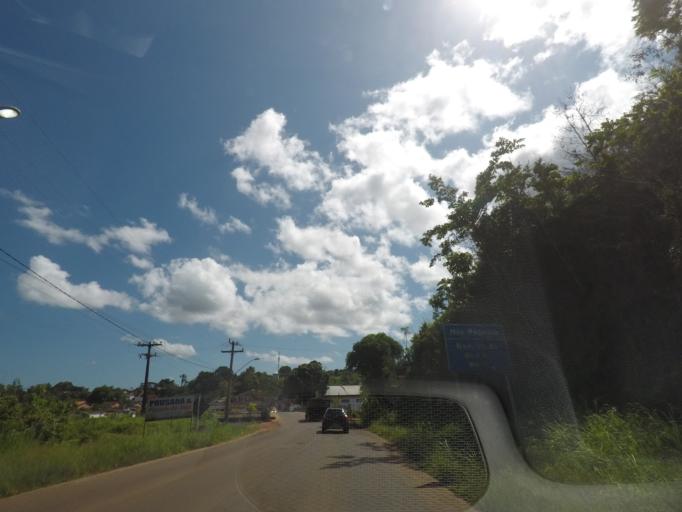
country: BR
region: Bahia
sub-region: Taperoa
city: Taperoa
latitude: -13.5979
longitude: -39.1056
